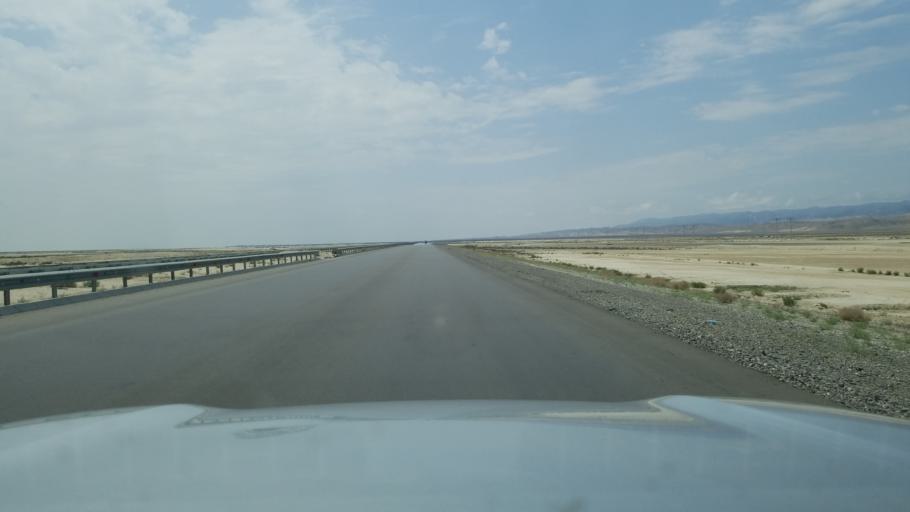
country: TM
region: Balkan
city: Gazanjyk
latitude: 39.2746
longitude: 55.1699
